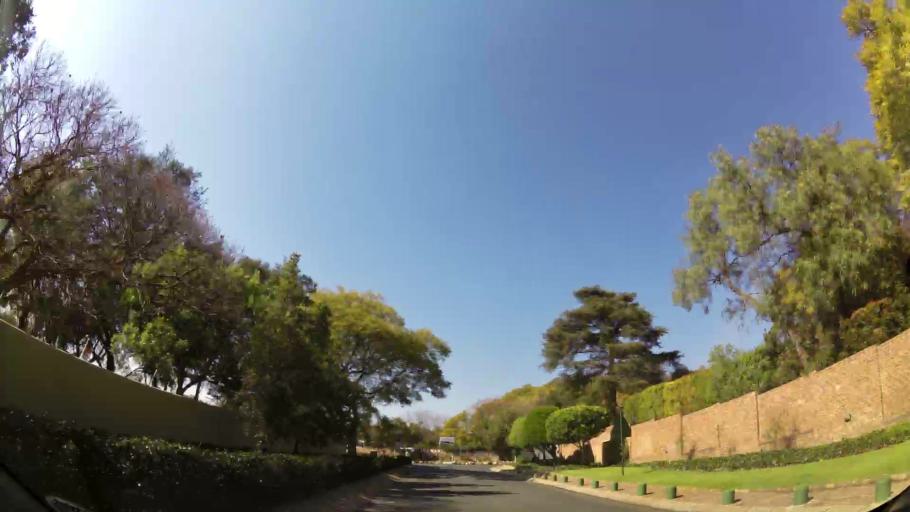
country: ZA
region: Gauteng
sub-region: City of Johannesburg Metropolitan Municipality
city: Johannesburg
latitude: -26.1090
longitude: 28.0361
